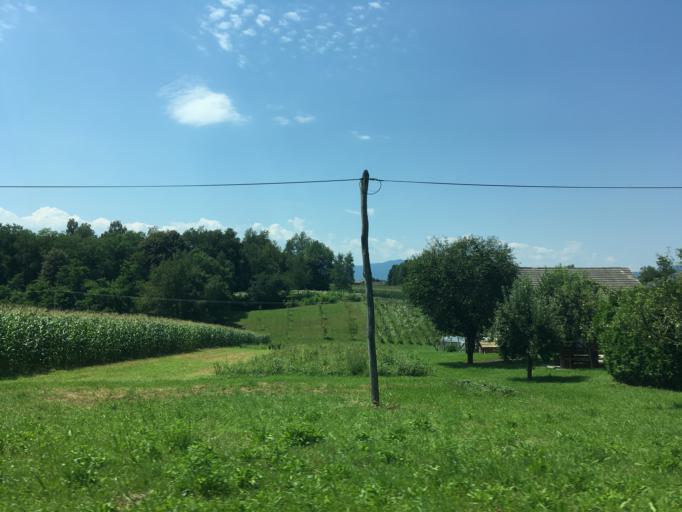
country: SI
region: Metlika
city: Metlika
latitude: 45.6249
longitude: 15.3205
